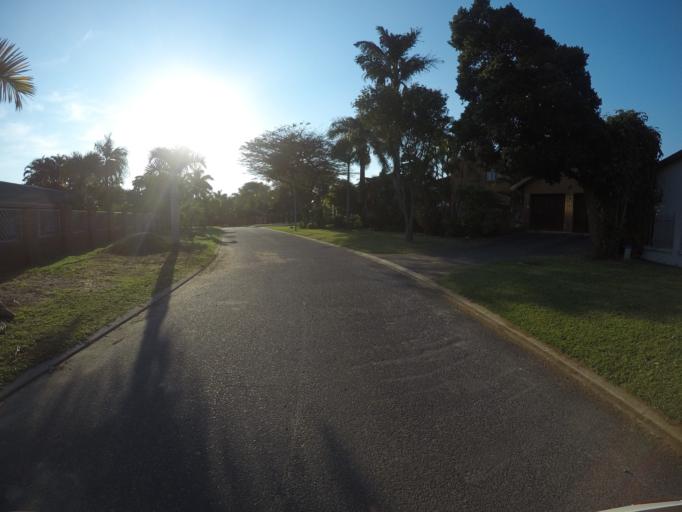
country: ZA
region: KwaZulu-Natal
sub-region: uThungulu District Municipality
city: Richards Bay
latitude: -28.7727
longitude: 32.1165
